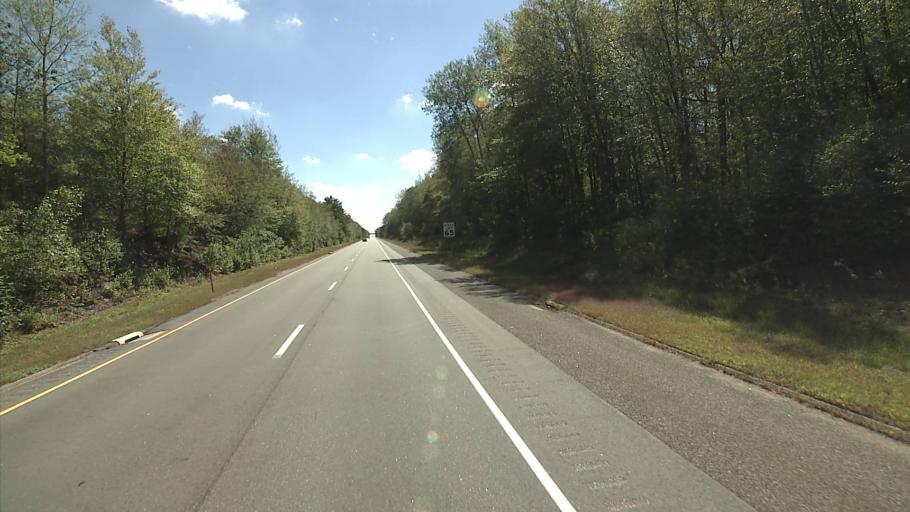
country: US
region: Connecticut
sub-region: New London County
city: Colchester
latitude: 41.5483
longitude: -72.3175
